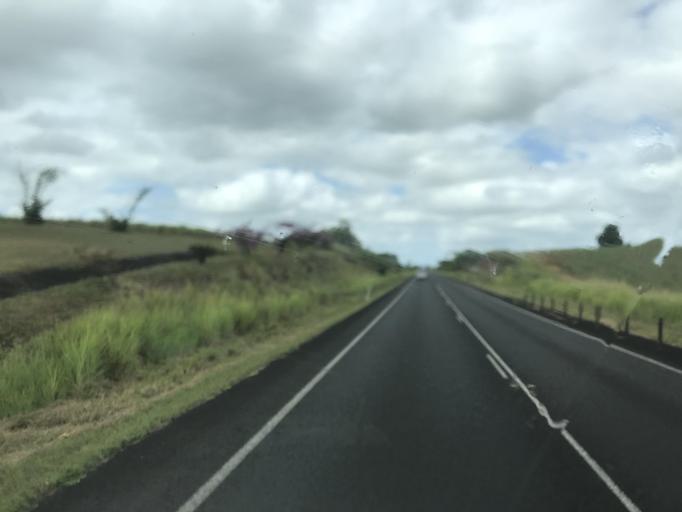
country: AU
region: Queensland
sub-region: Cassowary Coast
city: Innisfail
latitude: -17.5788
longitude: 145.9834
